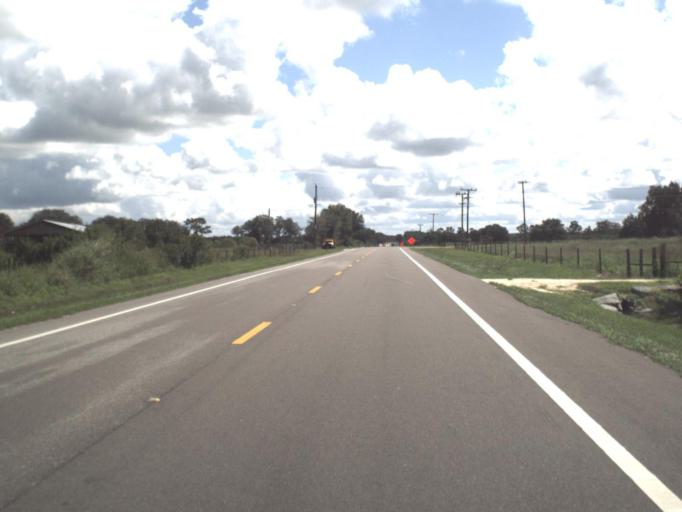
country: US
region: Florida
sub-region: Sarasota County
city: Lake Sarasota
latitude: 27.3726
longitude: -82.2208
